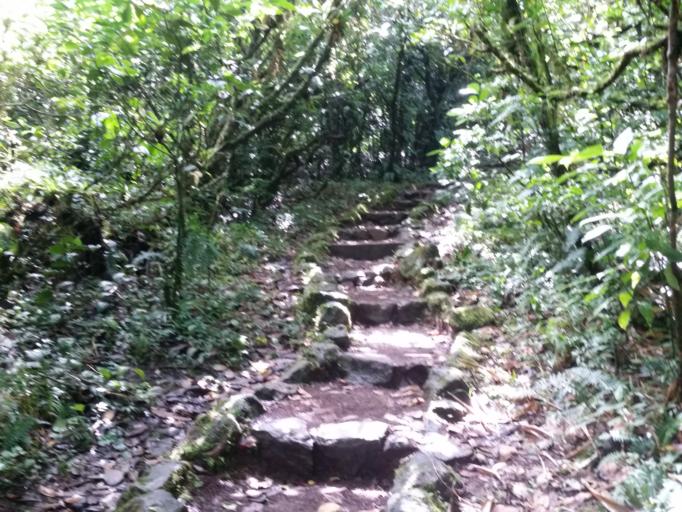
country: NI
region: Granada
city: Diriomo
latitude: 11.8341
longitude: -85.9783
